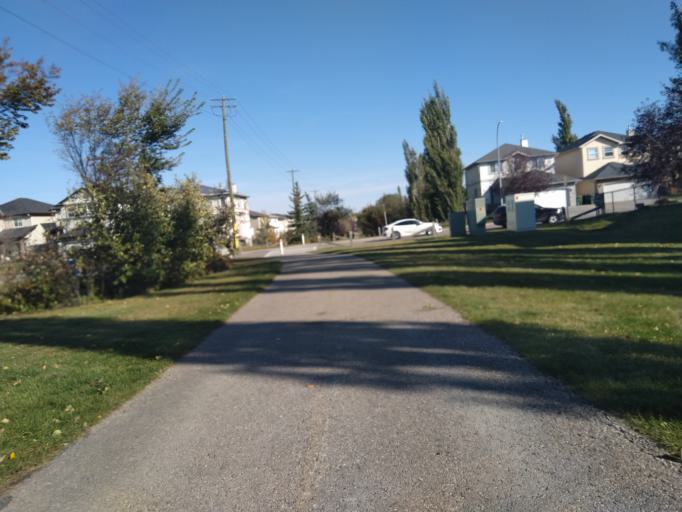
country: CA
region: Alberta
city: Calgary
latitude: 51.1541
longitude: -114.0863
